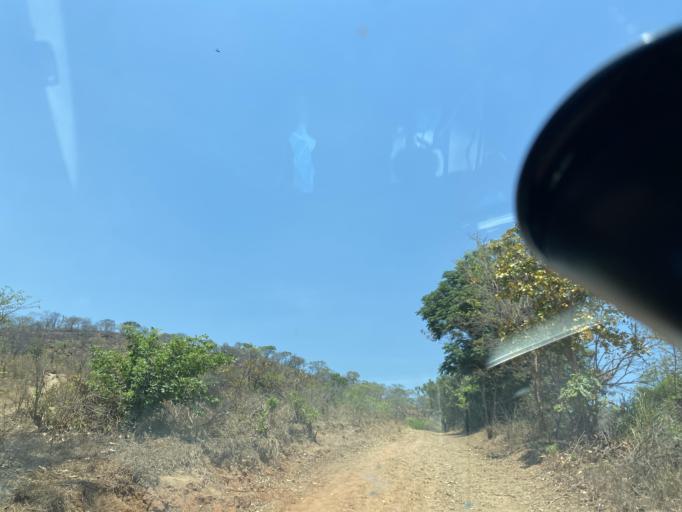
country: ZM
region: Lusaka
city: Kafue
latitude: -15.8069
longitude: 28.4347
